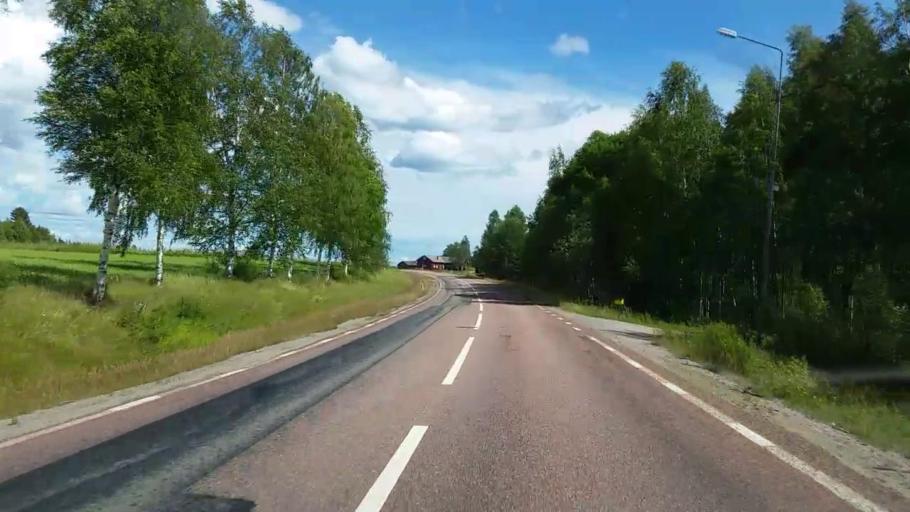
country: SE
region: Gaevleborg
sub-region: Ovanakers Kommun
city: Edsbyn
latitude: 61.3459
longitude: 15.6283
